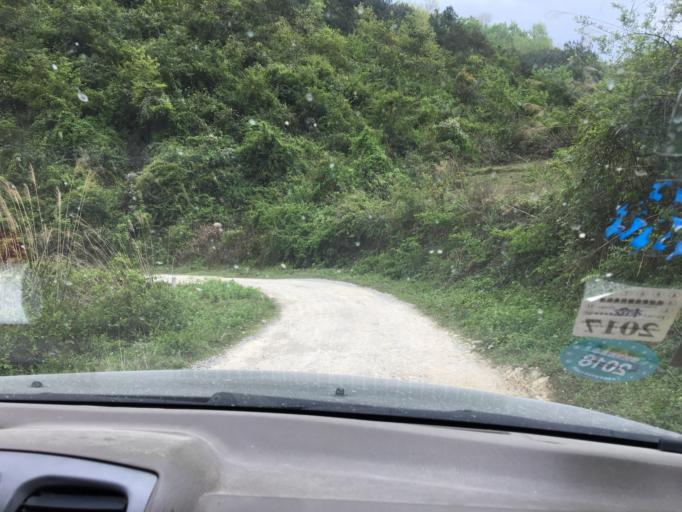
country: CN
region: Guizhou Sheng
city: Donghua
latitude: 28.0484
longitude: 108.0691
